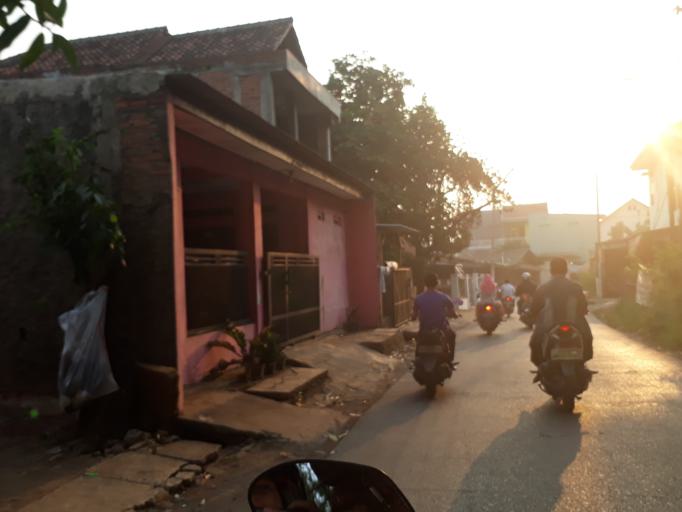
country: ID
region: West Java
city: Bekasi
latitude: -6.2459
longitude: 107.0581
